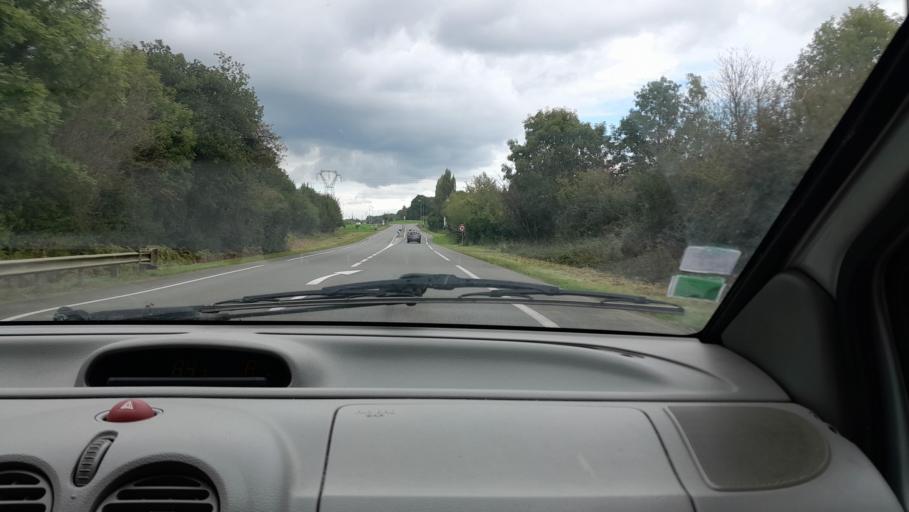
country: FR
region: Pays de la Loire
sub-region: Departement de la Mayenne
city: Montigne-le-Brillant
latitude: 48.0288
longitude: -0.8092
